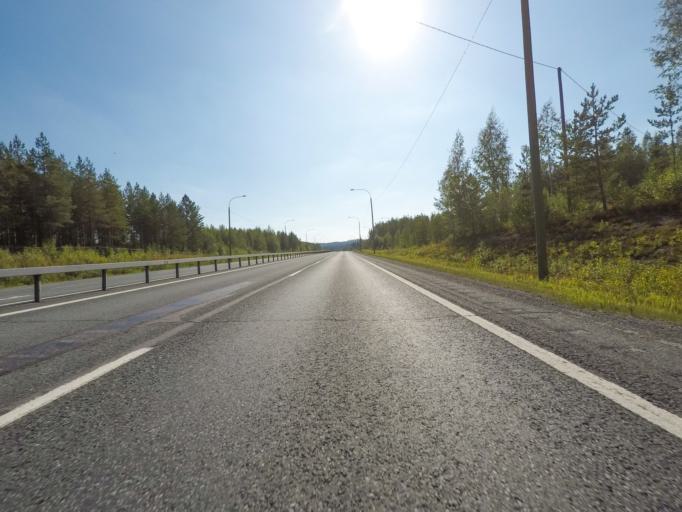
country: FI
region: Northern Savo
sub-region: Kuopio
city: Kuopio
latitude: 62.7147
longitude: 27.5744
